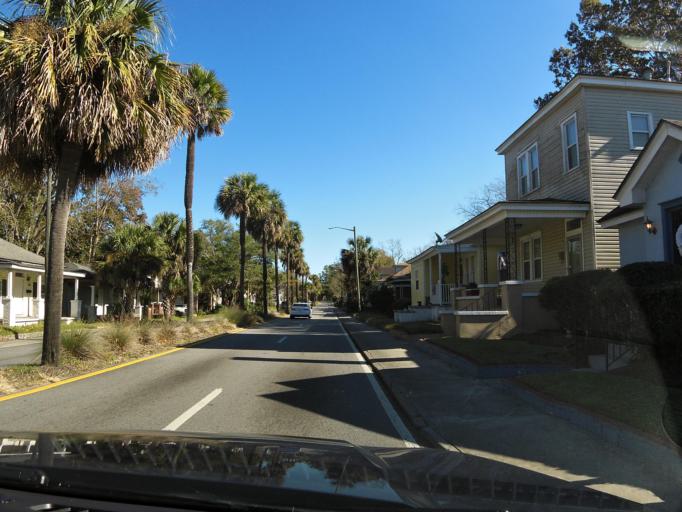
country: US
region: Georgia
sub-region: Chatham County
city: Savannah
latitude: 32.0555
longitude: -81.1134
